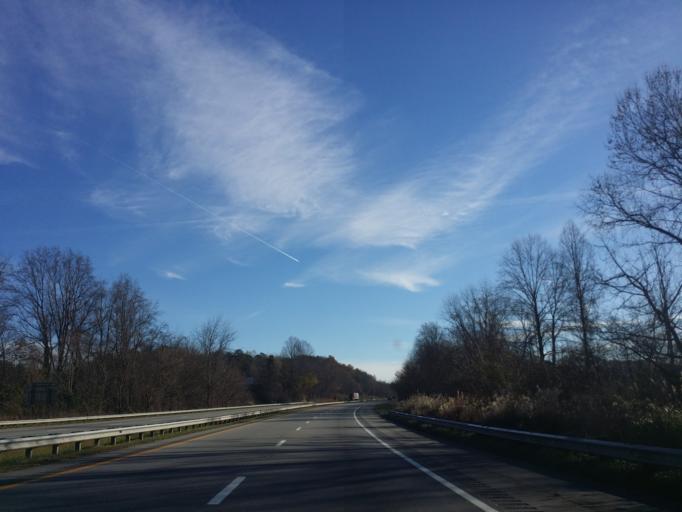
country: US
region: North Carolina
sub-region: McDowell County
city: West Marion
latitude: 35.6381
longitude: -82.1575
